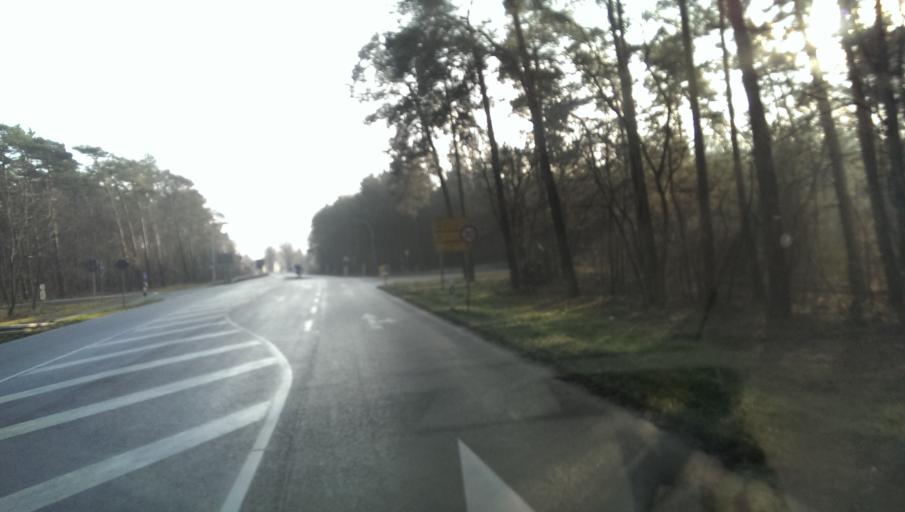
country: DE
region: Brandenburg
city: Bad Liebenwerda
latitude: 51.5526
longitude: 13.3785
